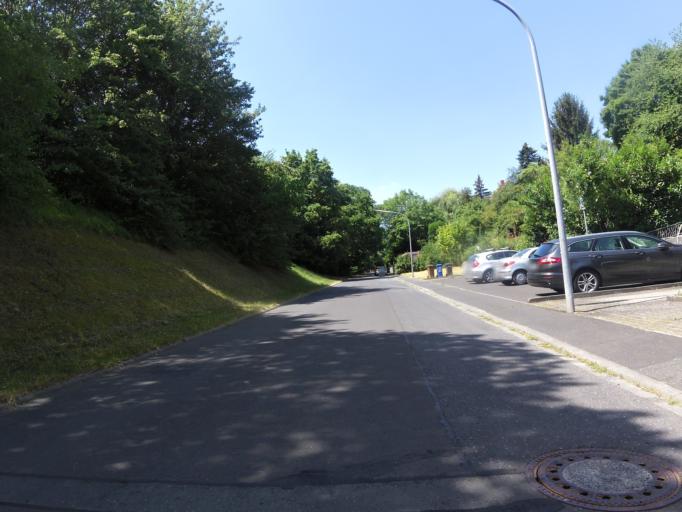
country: DE
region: Bavaria
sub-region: Regierungsbezirk Unterfranken
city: Wuerzburg
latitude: 49.8139
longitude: 9.9536
